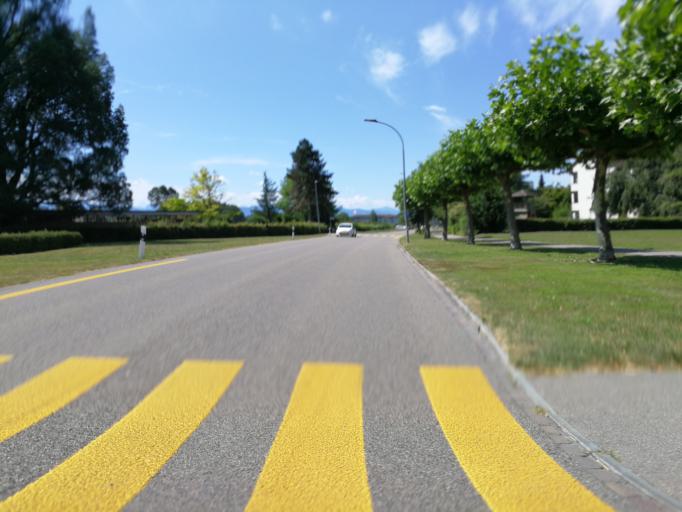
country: CH
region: Zurich
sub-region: Bezirk Hinwil
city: Wetzikon / Kempten
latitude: 47.3280
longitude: 8.8119
